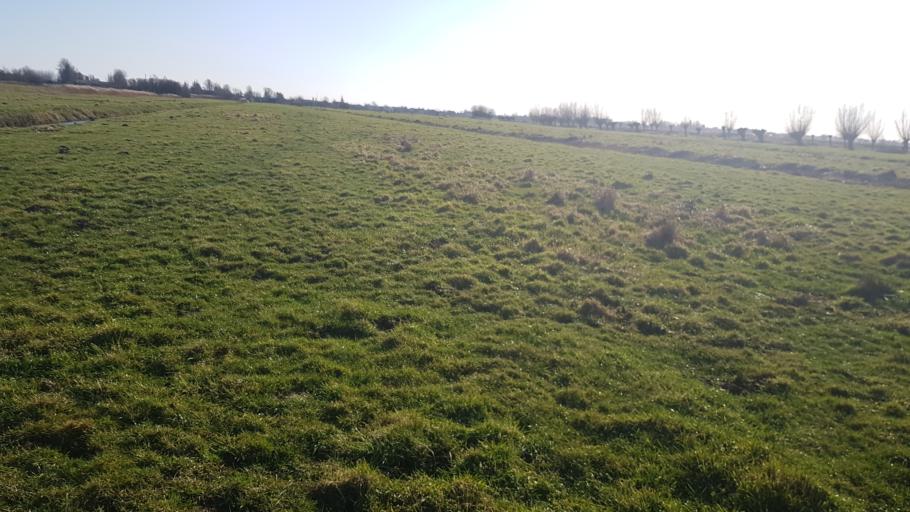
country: NL
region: South Holland
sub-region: Molenwaard
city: Nieuw-Lekkerland
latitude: 51.9200
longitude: 4.7483
